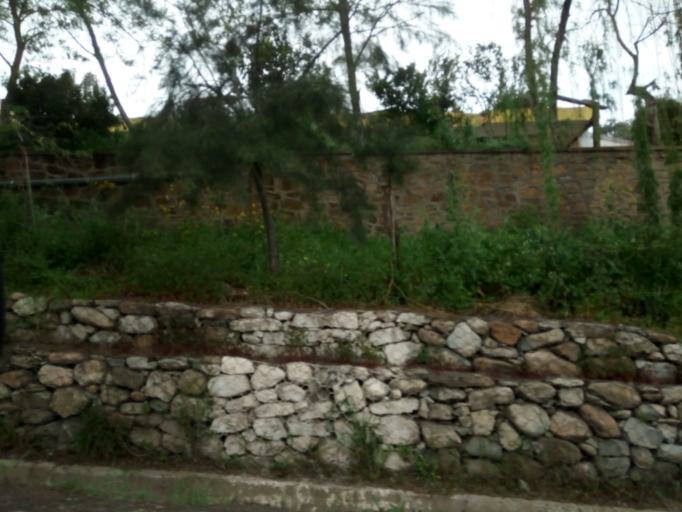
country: DZ
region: Medea
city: Medea
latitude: 36.2789
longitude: 2.7763
